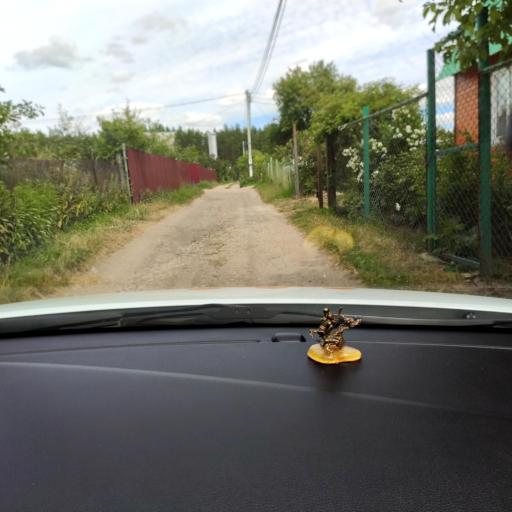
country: RU
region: Tatarstan
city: Staroye Arakchino
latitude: 55.8917
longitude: 49.0438
